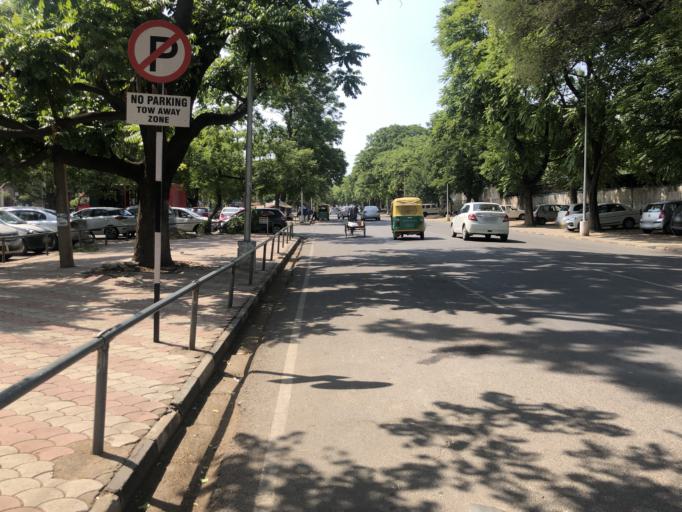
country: IN
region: Chandigarh
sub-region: Chandigarh
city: Chandigarh
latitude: 30.6939
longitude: 76.7716
